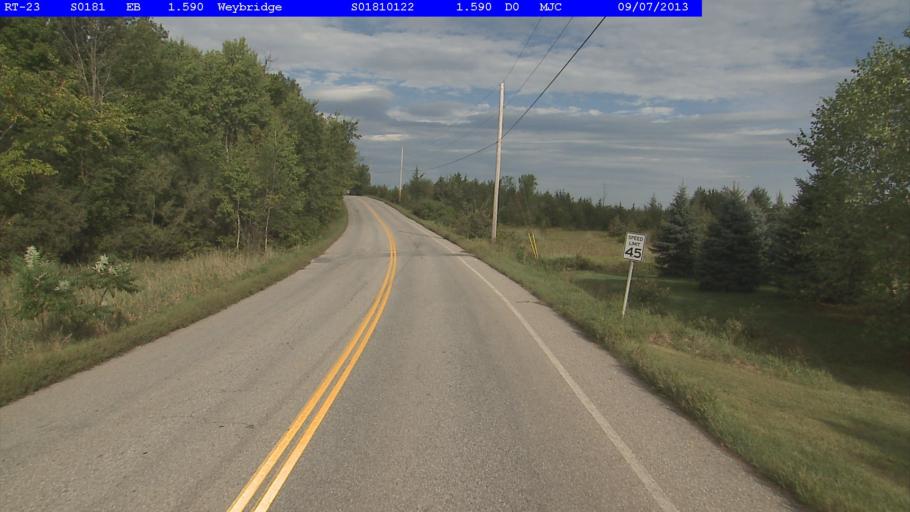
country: US
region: Vermont
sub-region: Addison County
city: Middlebury (village)
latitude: 44.0345
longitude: -73.2052
